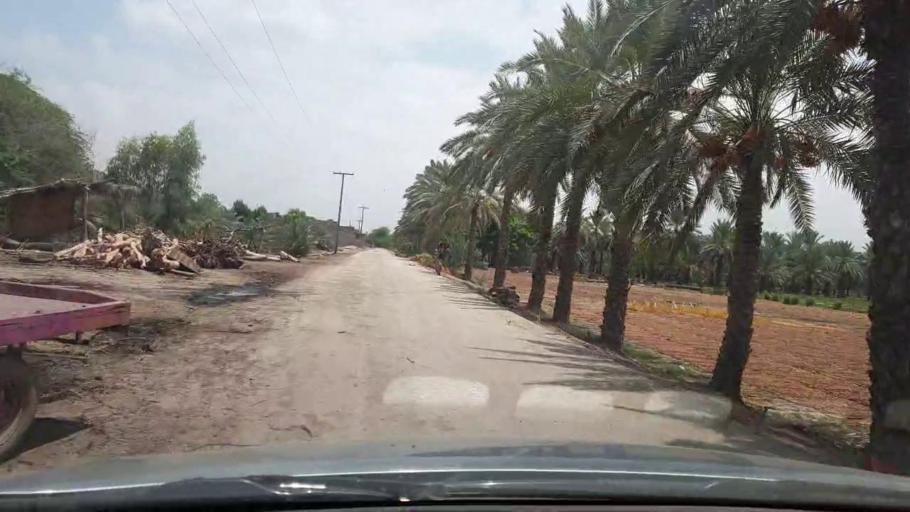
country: PK
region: Sindh
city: Khairpur
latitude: 27.4366
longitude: 68.7583
